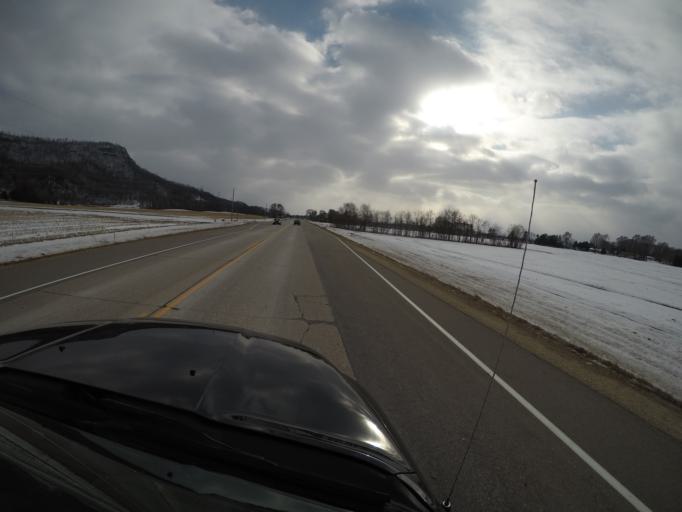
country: US
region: Wisconsin
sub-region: La Crosse County
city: Holmen
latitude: 44.0166
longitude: -91.2881
